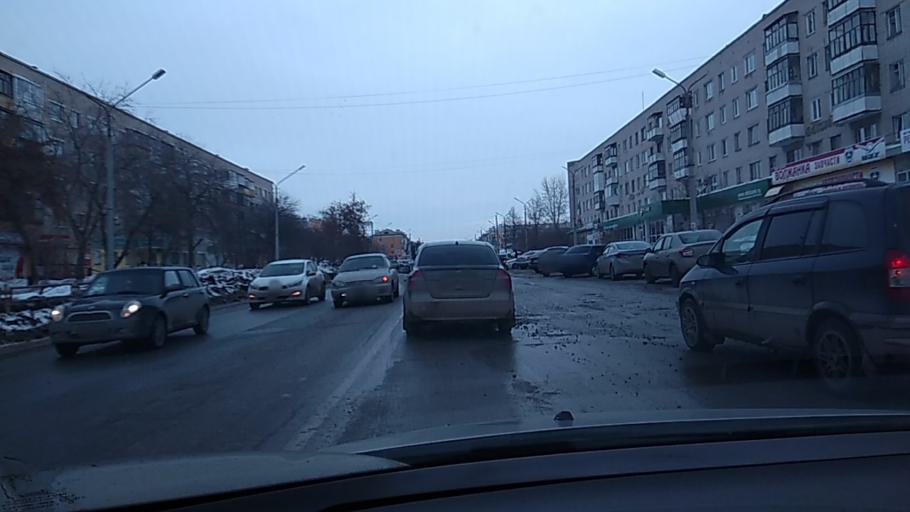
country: RU
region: Sverdlovsk
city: Kamensk-Ural'skiy
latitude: 56.4212
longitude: 61.9134
